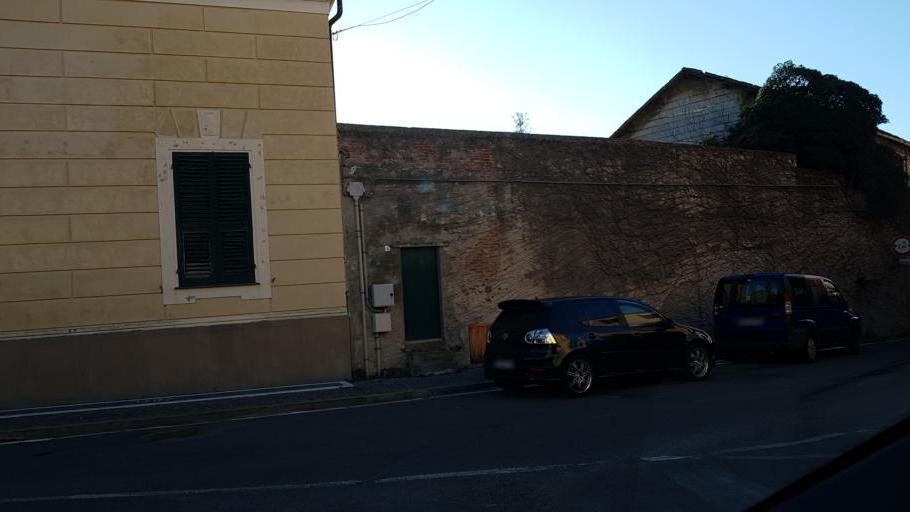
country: IT
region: Liguria
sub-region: Provincia di Savona
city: Valleggia
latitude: 44.2949
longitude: 8.4526
